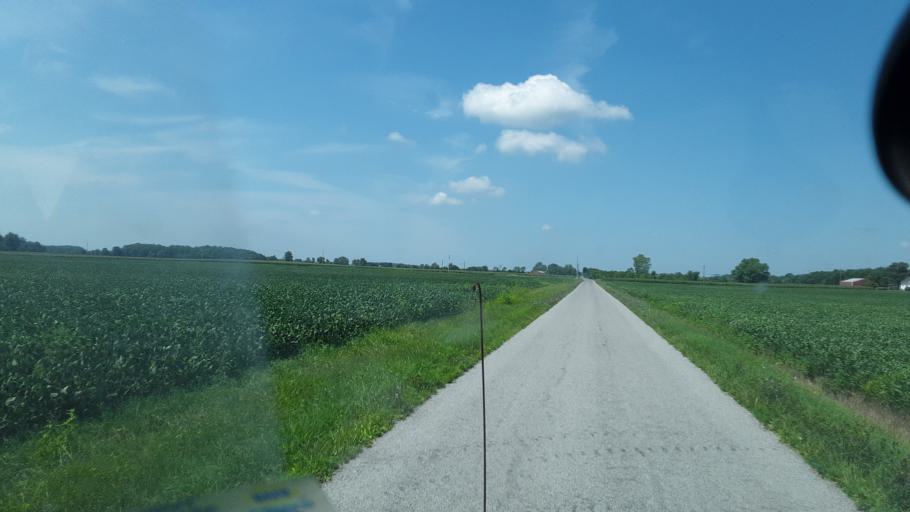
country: US
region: Ohio
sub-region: Hancock County
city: Findlay
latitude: 40.9715
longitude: -83.5698
